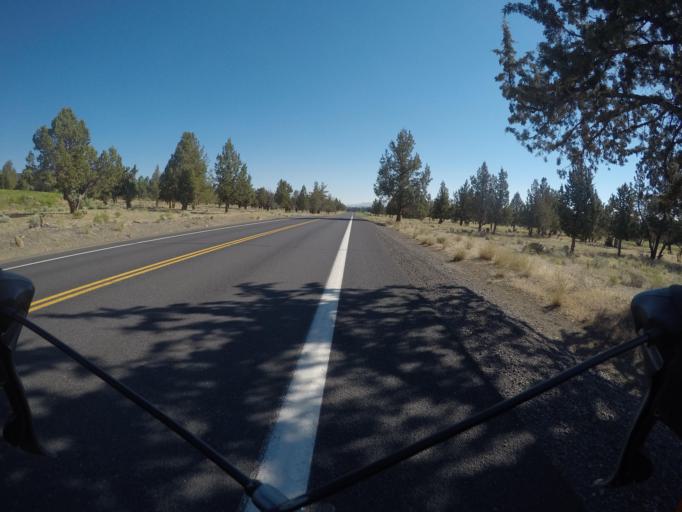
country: US
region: Oregon
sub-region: Deschutes County
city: Redmond
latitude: 44.2573
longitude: -121.2684
